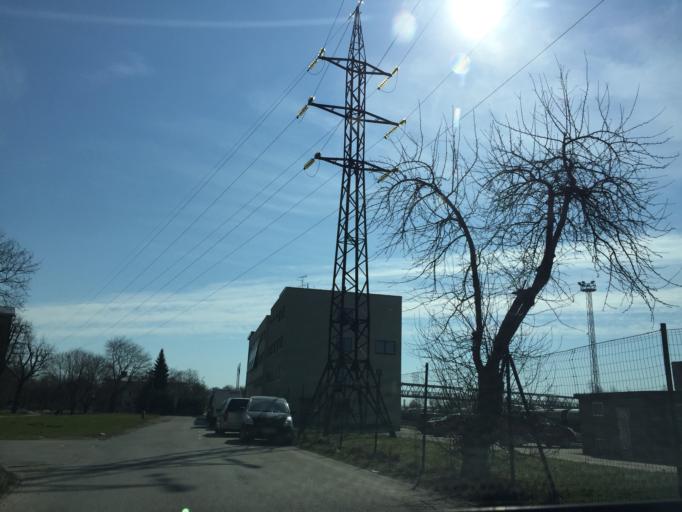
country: EE
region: Ida-Virumaa
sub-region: Narva linn
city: Narva
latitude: 59.3703
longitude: 28.1943
